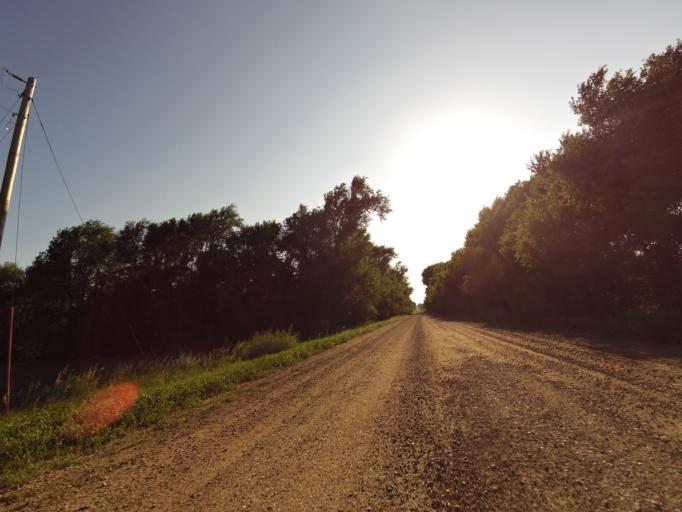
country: US
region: Kansas
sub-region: McPherson County
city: Inman
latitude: 38.1883
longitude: -97.8642
